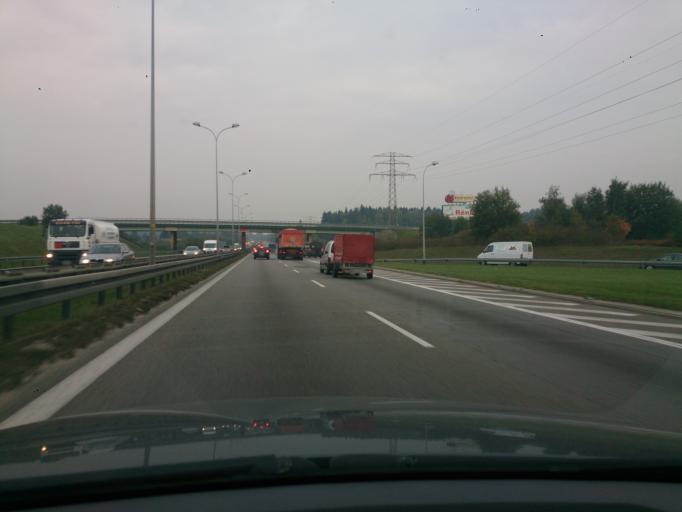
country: PL
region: Pomeranian Voivodeship
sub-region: Gdynia
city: Wielki Kack
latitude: 54.4130
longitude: 18.4864
